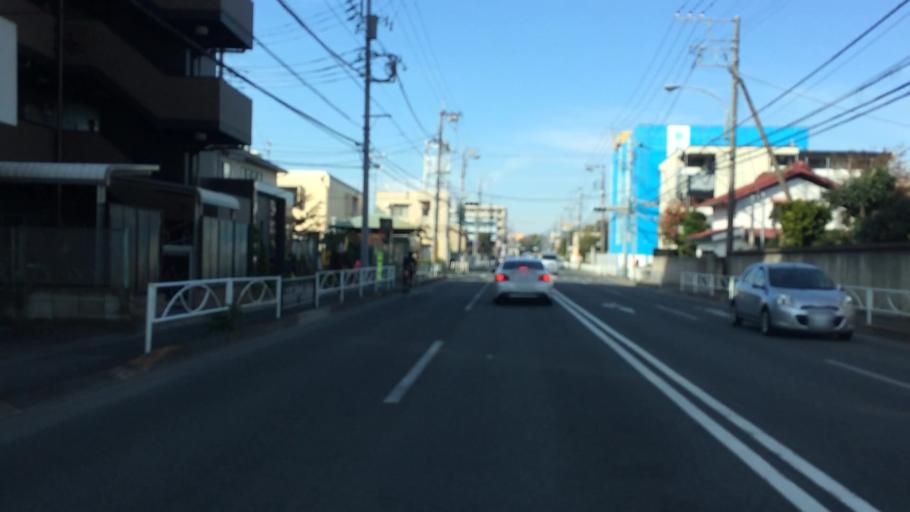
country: JP
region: Tokyo
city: Hino
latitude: 35.6833
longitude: 139.4245
